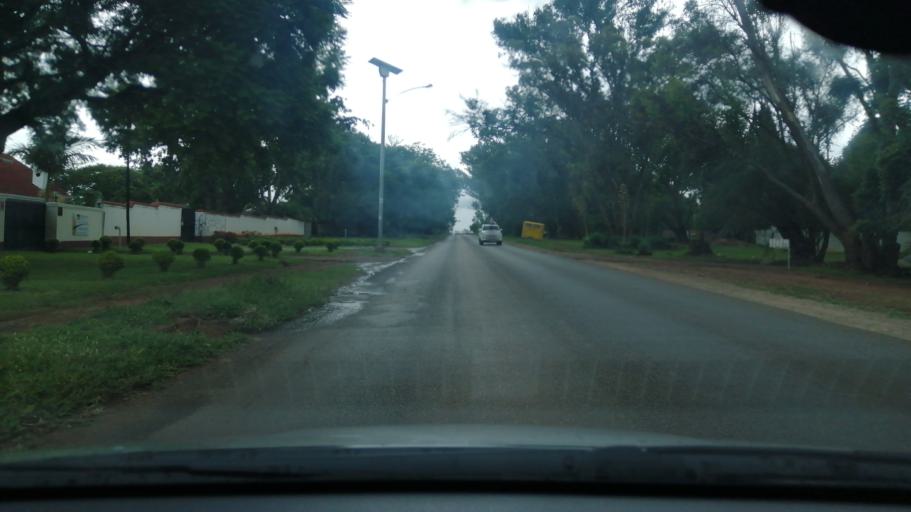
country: ZW
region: Harare
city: Harare
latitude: -17.7966
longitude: 31.0705
